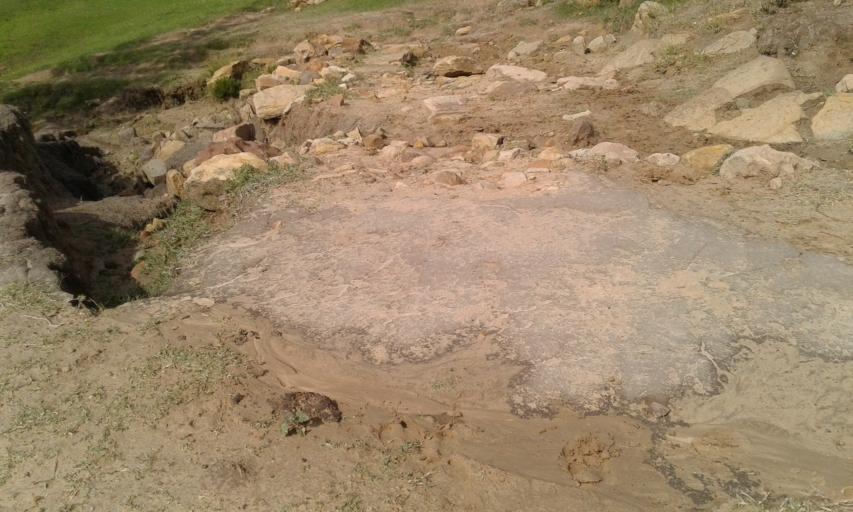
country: LS
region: Maseru
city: Maseru
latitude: -29.4245
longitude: 27.5760
